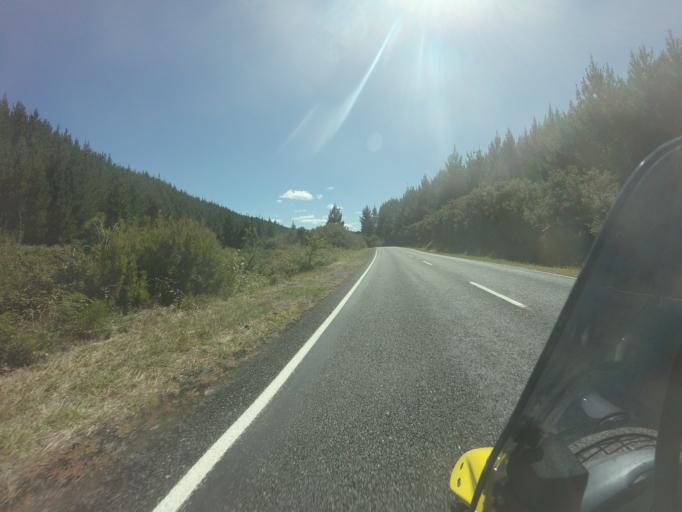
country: NZ
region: Bay of Plenty
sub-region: Whakatane District
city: Murupara
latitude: -38.2892
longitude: 176.8117
